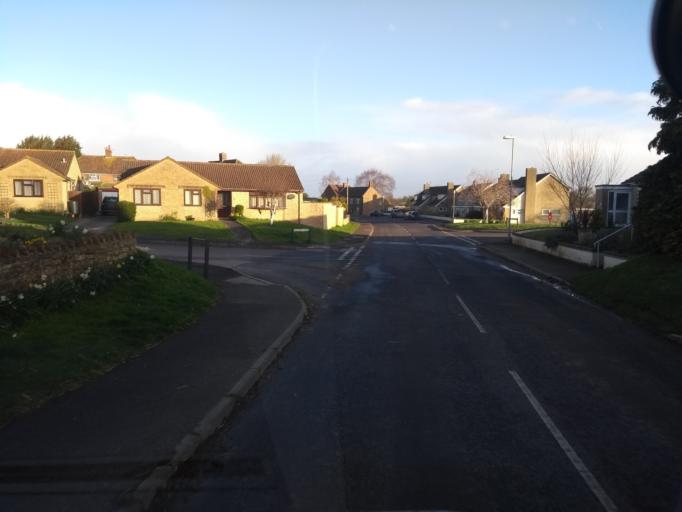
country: GB
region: England
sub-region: Somerset
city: Stoke-sub-Hamdon
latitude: 50.9590
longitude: -2.7505
